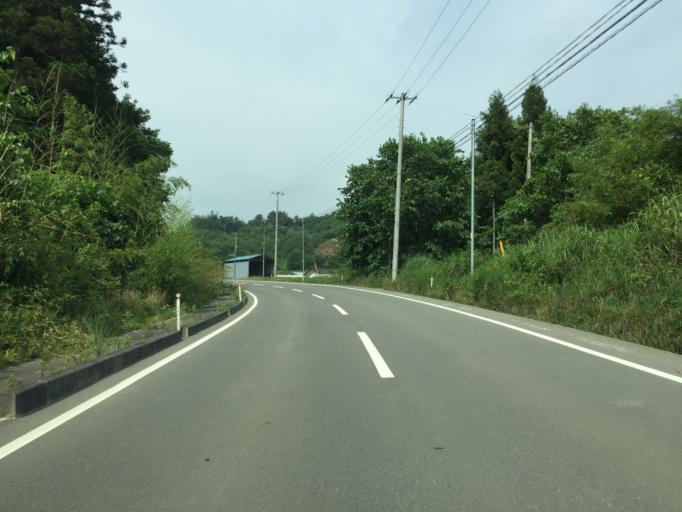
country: JP
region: Fukushima
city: Funehikimachi-funehiki
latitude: 37.4614
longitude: 140.7536
